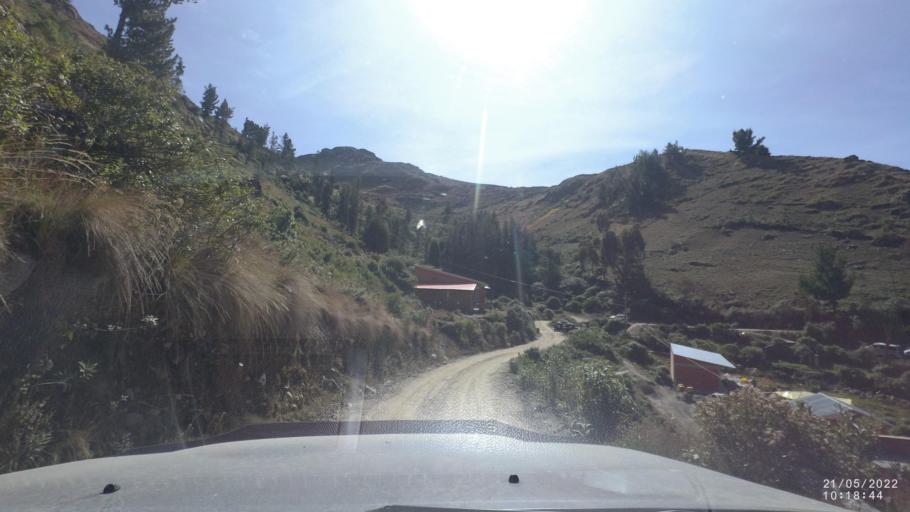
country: BO
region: Cochabamba
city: Colomi
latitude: -17.3264
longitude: -65.9604
